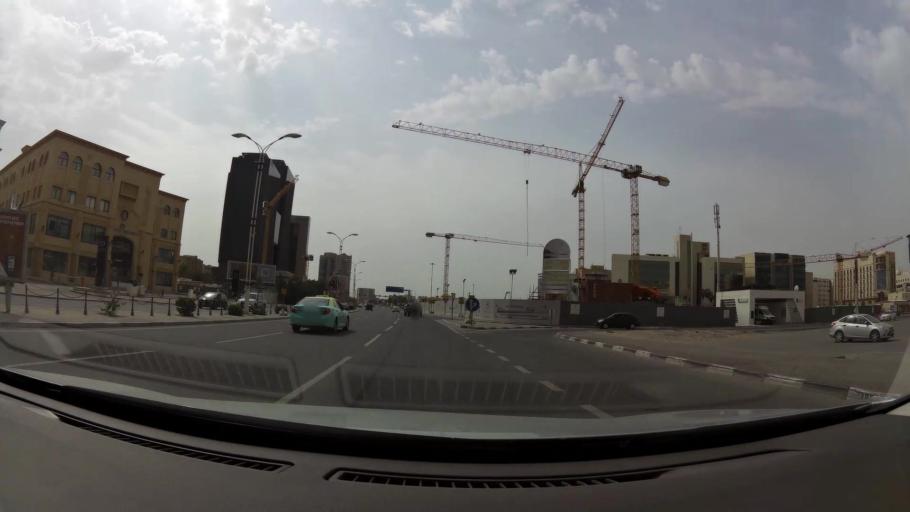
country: QA
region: Baladiyat ad Dawhah
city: Doha
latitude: 25.2838
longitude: 51.5057
